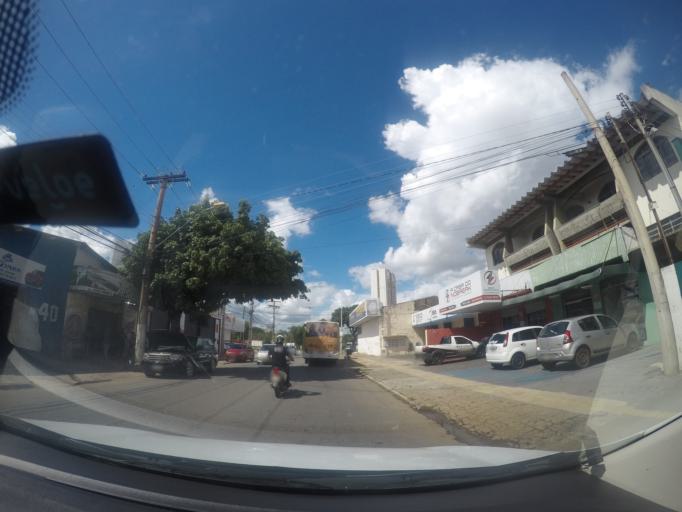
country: BR
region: Goias
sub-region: Goiania
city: Goiania
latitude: -16.6797
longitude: -49.2864
